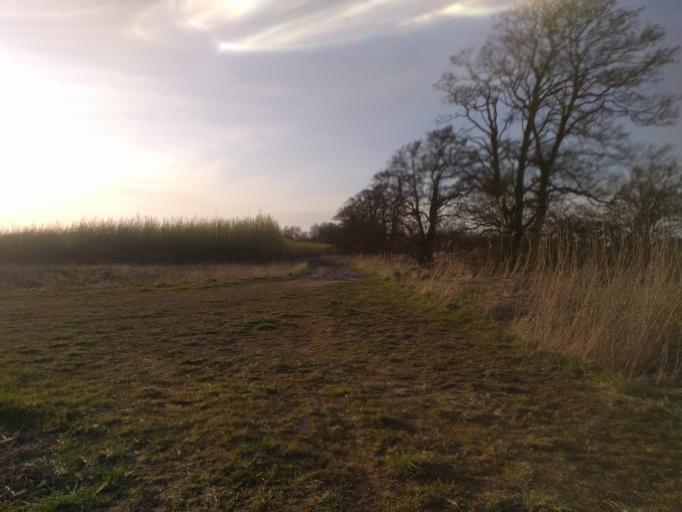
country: DK
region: South Denmark
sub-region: Kerteminde Kommune
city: Munkebo
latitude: 55.4121
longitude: 10.5499
